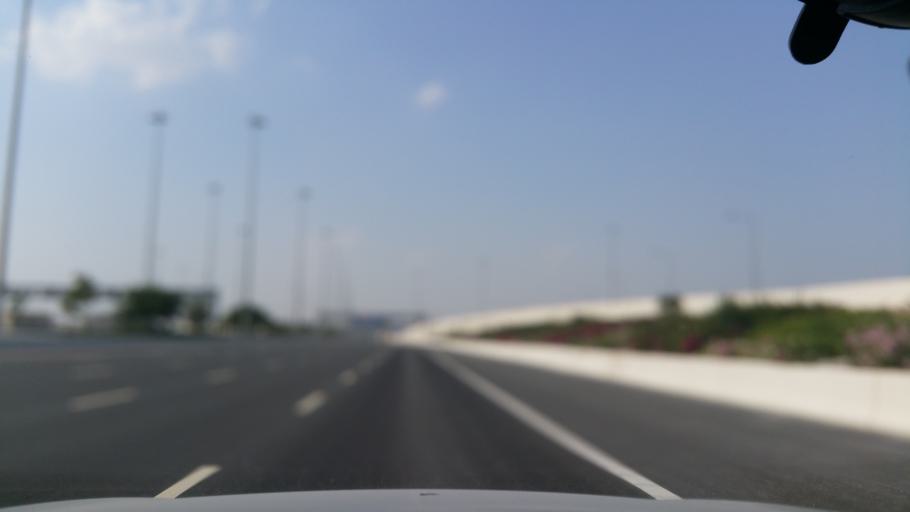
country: QA
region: Baladiyat Umm Salal
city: Umm Salal Muhammad
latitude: 25.3942
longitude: 51.4971
